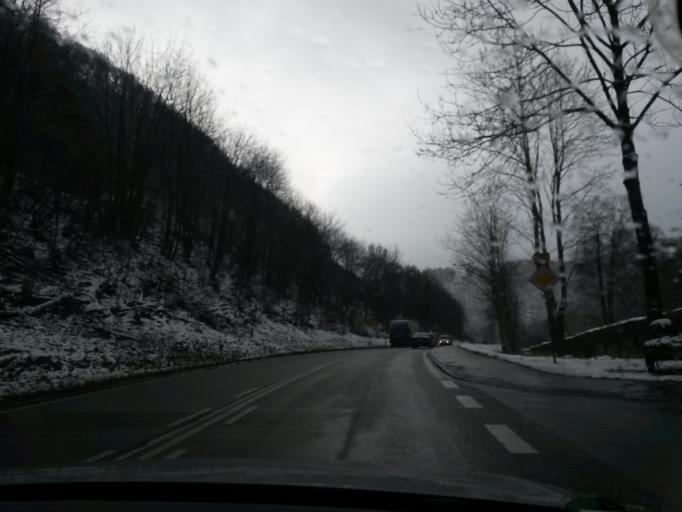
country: DE
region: Baden-Wuerttemberg
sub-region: Regierungsbezirk Stuttgart
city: Geislingen an der Steige
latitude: 48.6045
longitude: 9.8435
